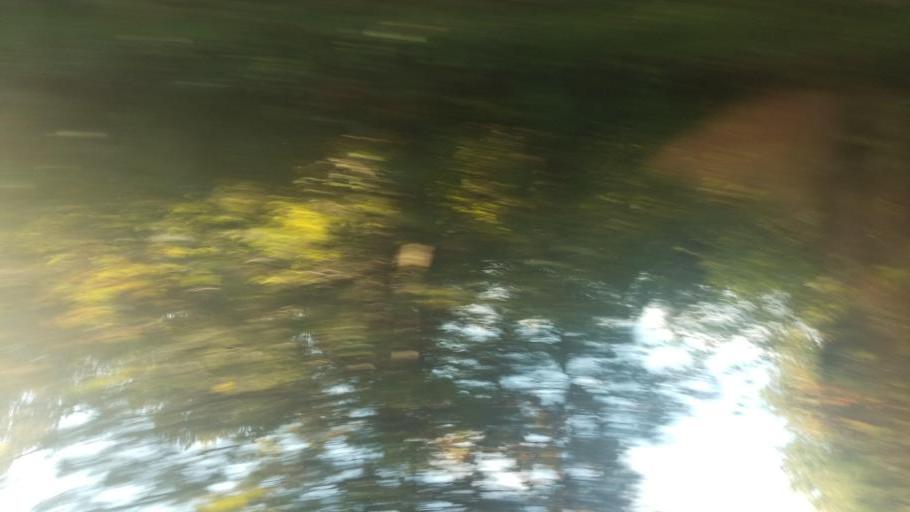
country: US
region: Illinois
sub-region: Williamson County
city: Marion
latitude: 37.7609
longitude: -88.8045
